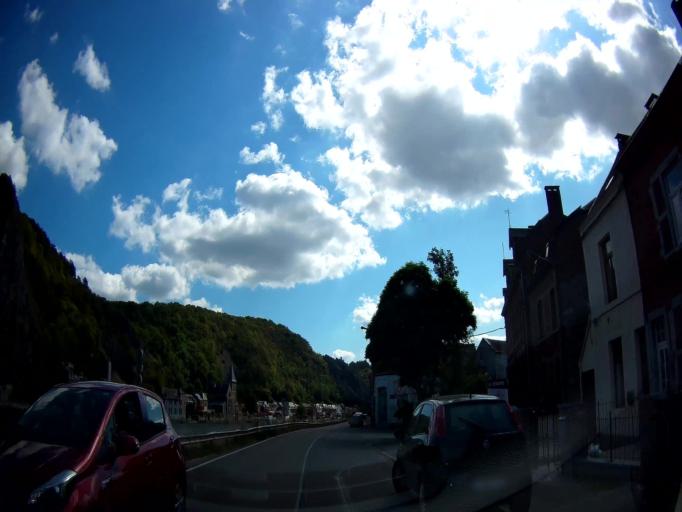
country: BE
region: Wallonia
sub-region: Province de Namur
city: Dinant
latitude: 50.2496
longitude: 4.9173
